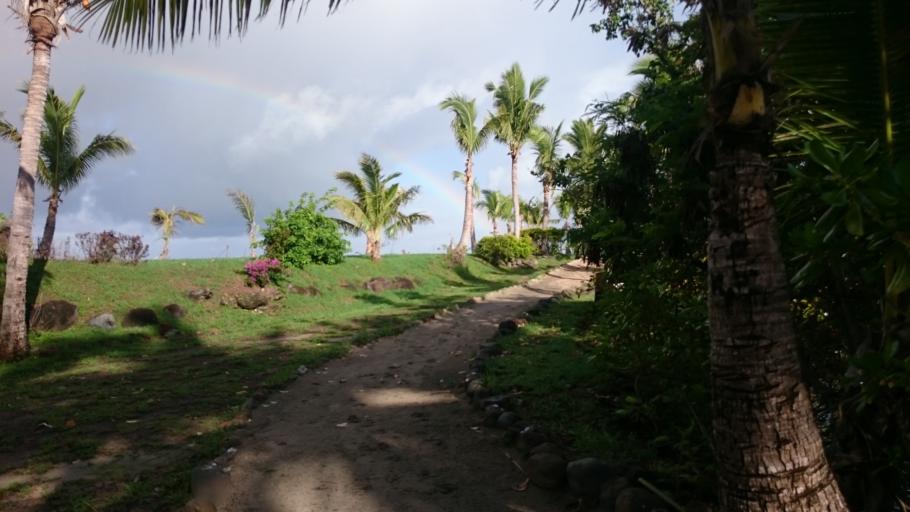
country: FJ
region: Western
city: Ba
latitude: -17.3192
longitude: 178.2042
